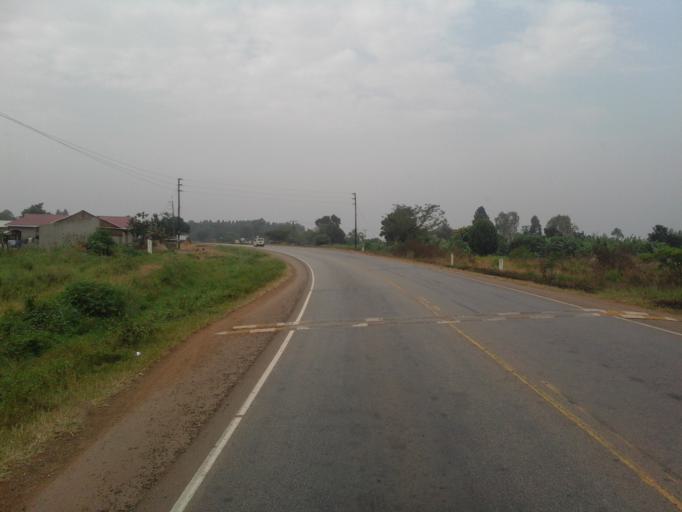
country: UG
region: Eastern Region
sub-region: Busia District
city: Busia
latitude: 0.6011
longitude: 34.0648
